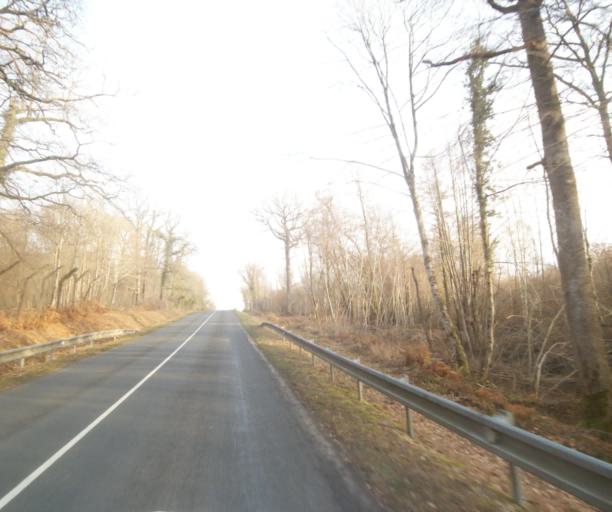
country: FR
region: Champagne-Ardenne
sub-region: Departement de la Haute-Marne
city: Chancenay
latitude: 48.6889
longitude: 4.9446
